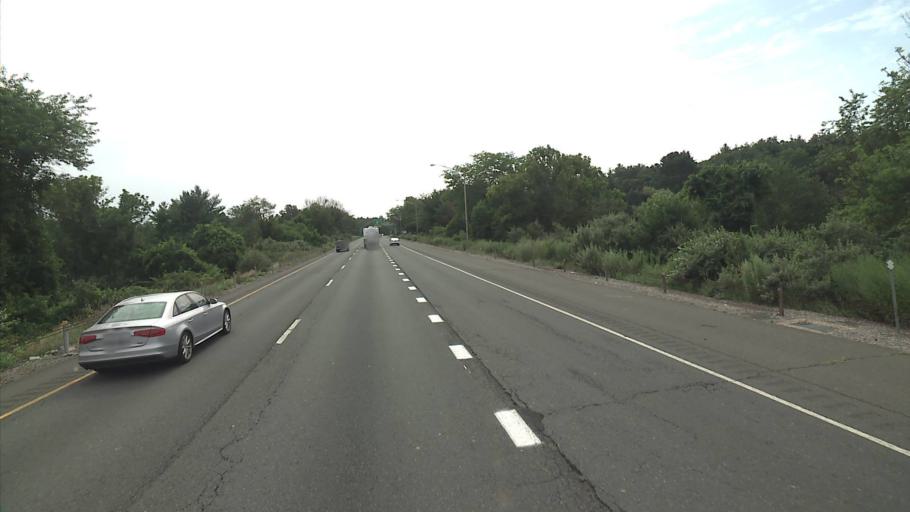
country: US
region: Connecticut
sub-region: Fairfield County
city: Newtown
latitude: 41.4147
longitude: -73.2768
